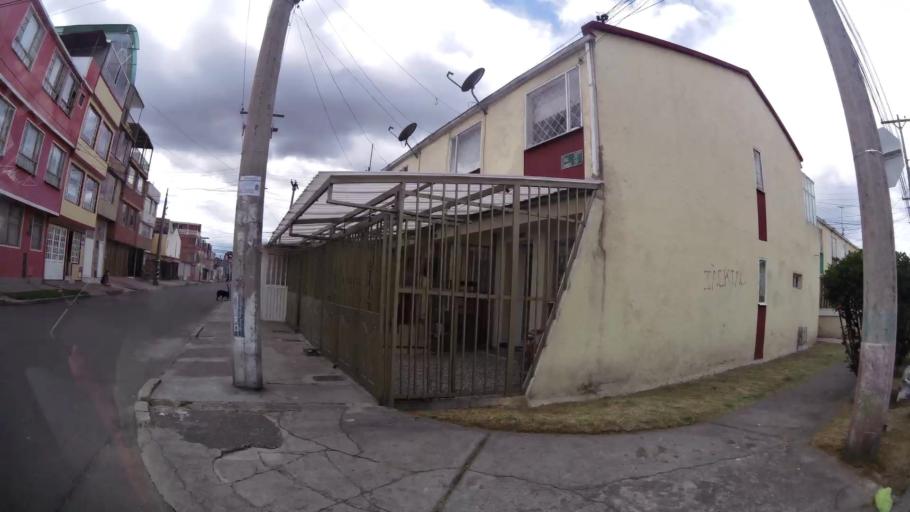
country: CO
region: Bogota D.C.
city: Bogota
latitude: 4.5974
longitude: -74.1204
